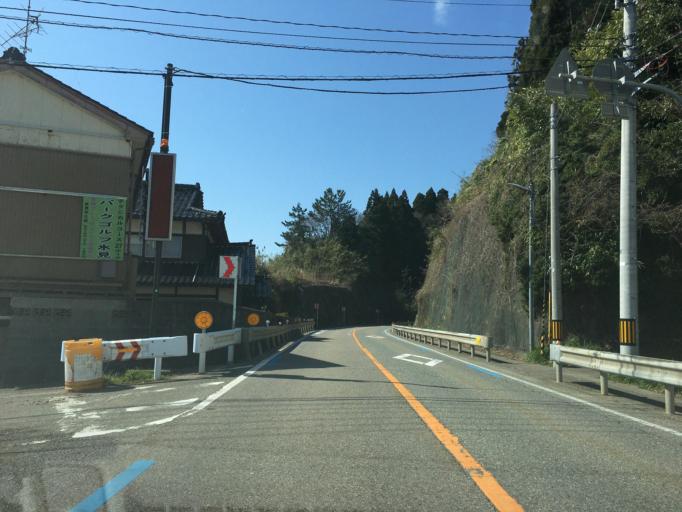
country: JP
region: Toyama
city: Himi
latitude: 36.8920
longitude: 137.0043
